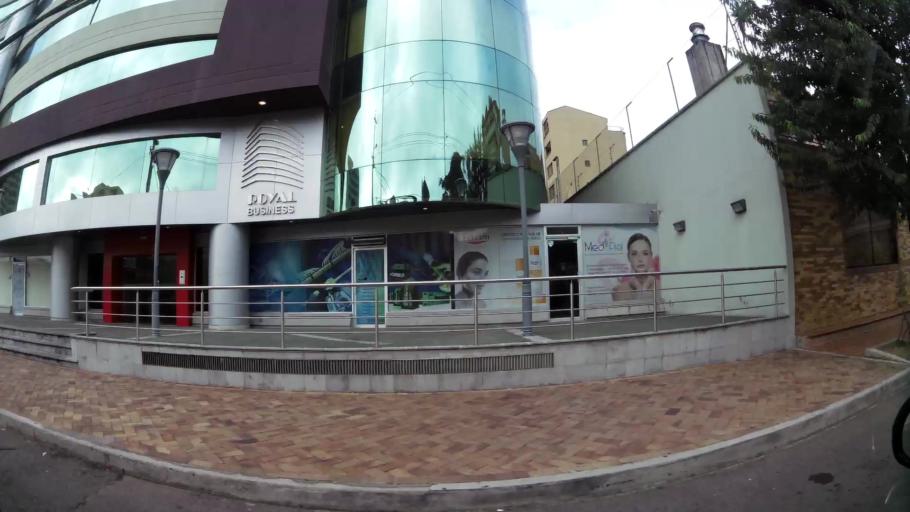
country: EC
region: Pichincha
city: Quito
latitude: -0.1991
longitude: -78.4868
